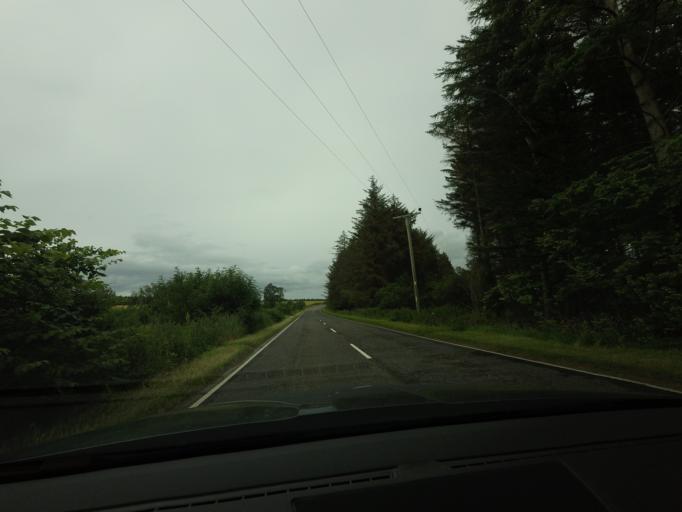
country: GB
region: Scotland
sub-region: Moray
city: Findochty
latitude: 57.6727
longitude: -2.9146
